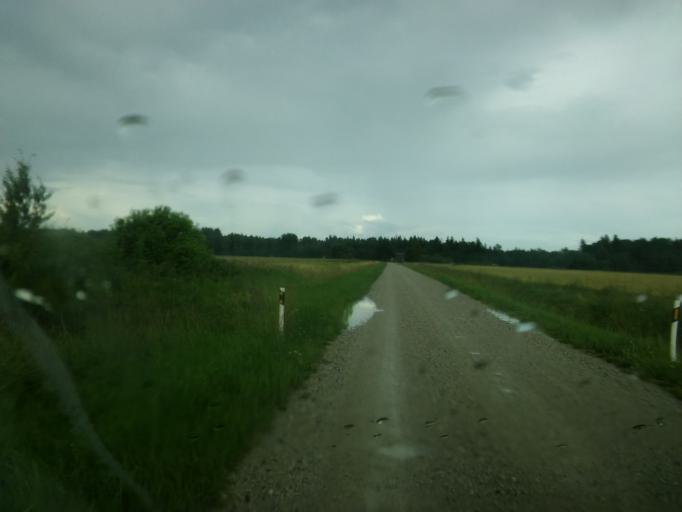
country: EE
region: Paernumaa
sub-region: Halinga vald
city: Parnu-Jaagupi
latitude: 58.7882
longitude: 24.5933
